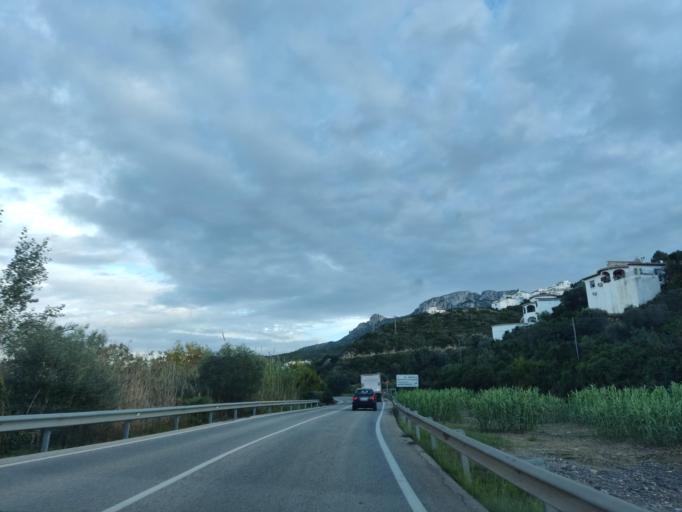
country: ES
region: Valencia
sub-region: Provincia de Alicante
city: Benimeli
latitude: 38.8528
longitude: -0.0456
